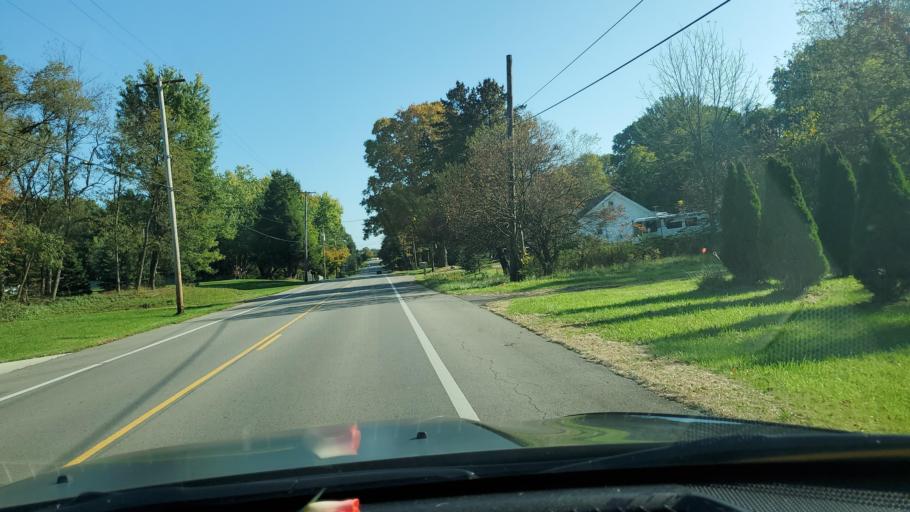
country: US
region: Ohio
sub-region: Trumbull County
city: Churchill
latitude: 41.1400
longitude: -80.6201
